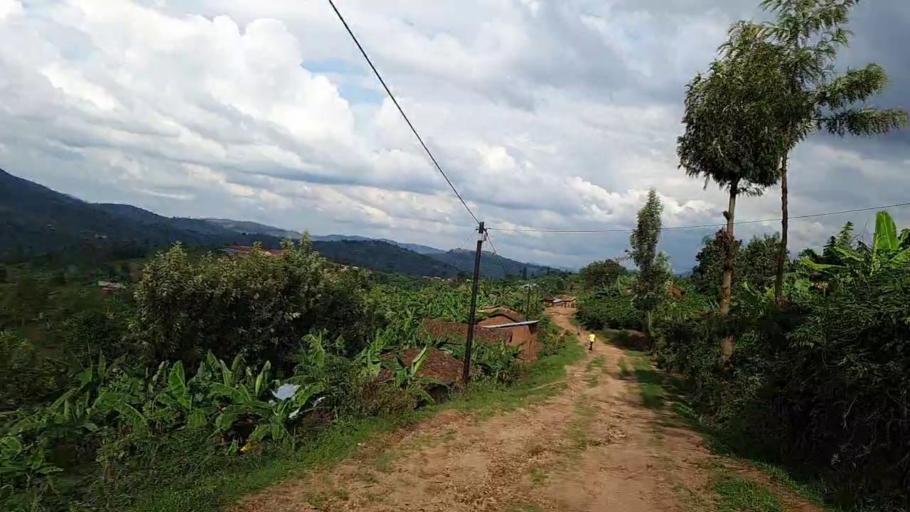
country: RW
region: Southern Province
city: Gikongoro
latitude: -2.4245
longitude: 29.6428
